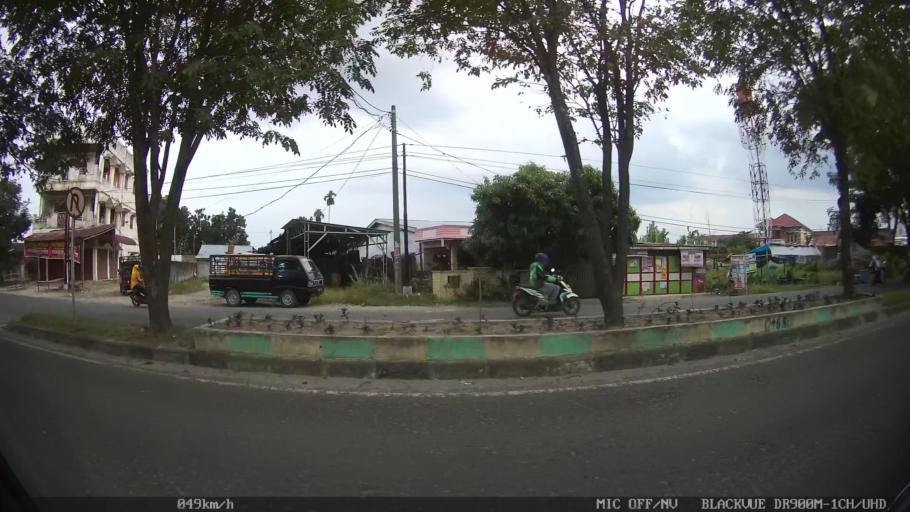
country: ID
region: North Sumatra
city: Sunggal
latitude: 3.5460
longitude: 98.6058
